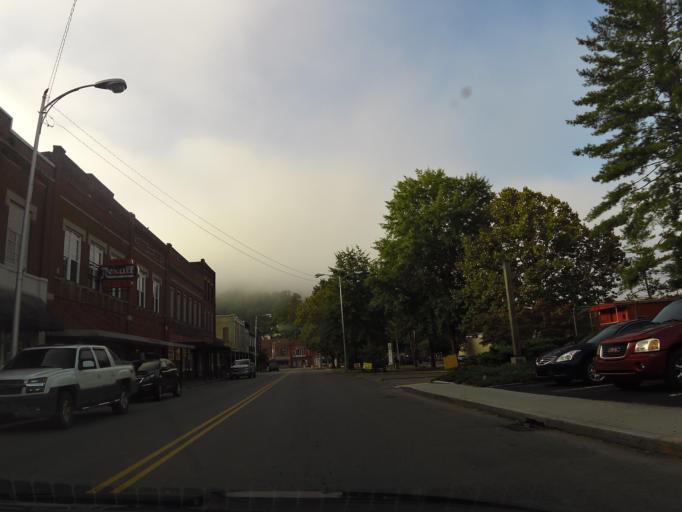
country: US
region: Tennessee
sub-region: Campbell County
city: Jellico
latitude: 36.5891
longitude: -84.1267
